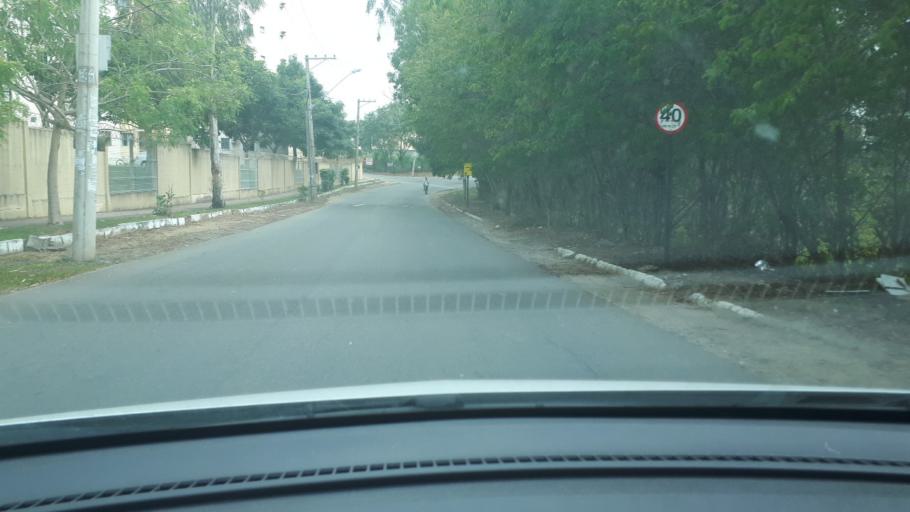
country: BR
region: Espirito Santo
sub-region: Serra
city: Serra
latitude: -20.1466
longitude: -40.1973
